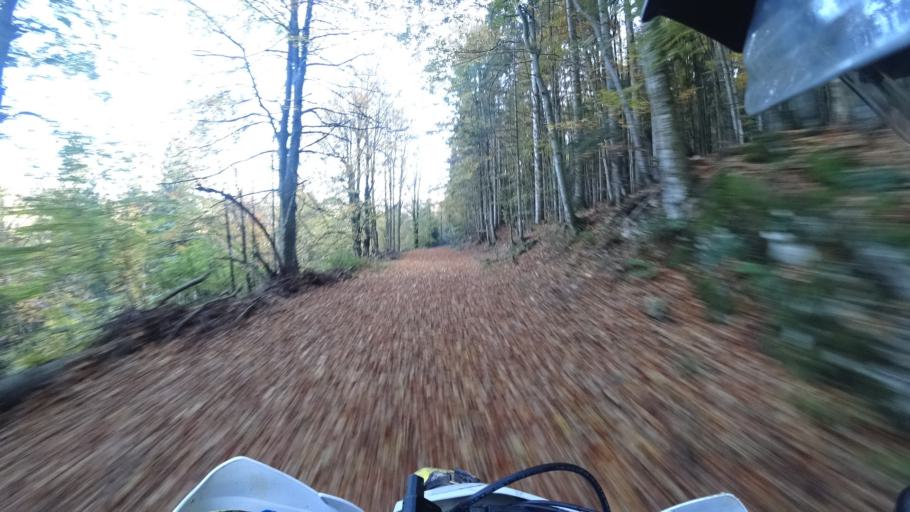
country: HR
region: Karlovacka
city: Plaski
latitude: 44.9401
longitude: 15.4580
